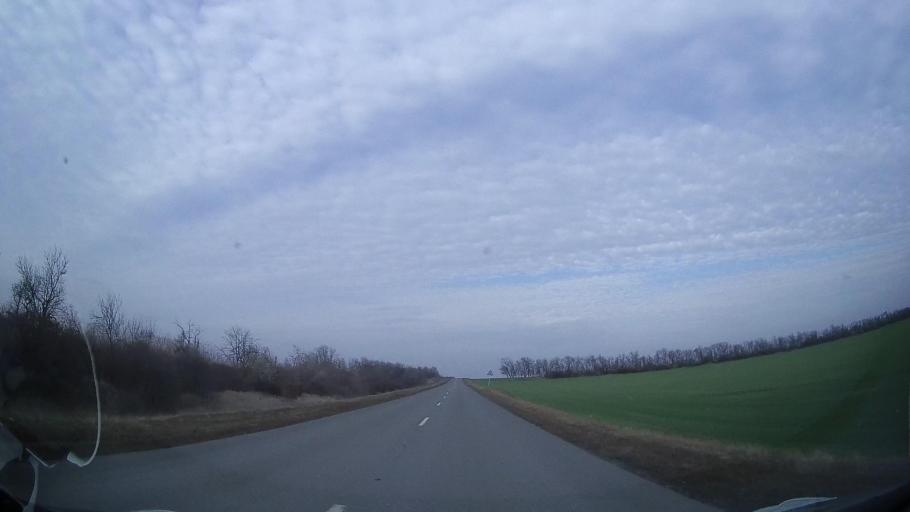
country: RU
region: Rostov
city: Zernograd
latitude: 46.9097
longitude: 40.3389
